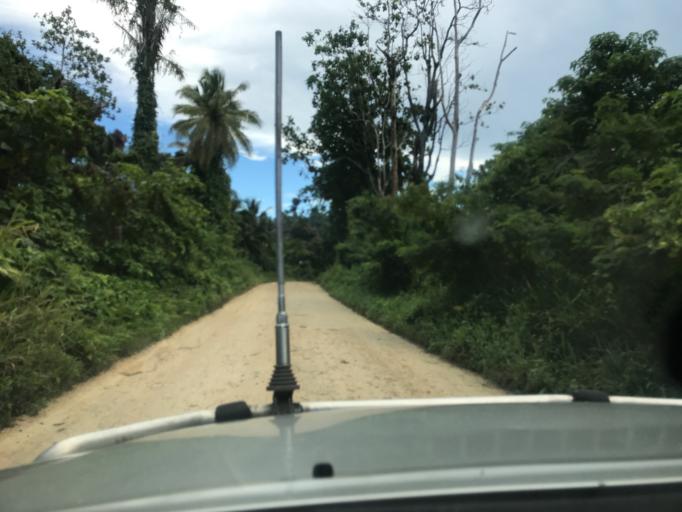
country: SB
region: Malaita
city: Auki
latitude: -8.6186
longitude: 160.6632
